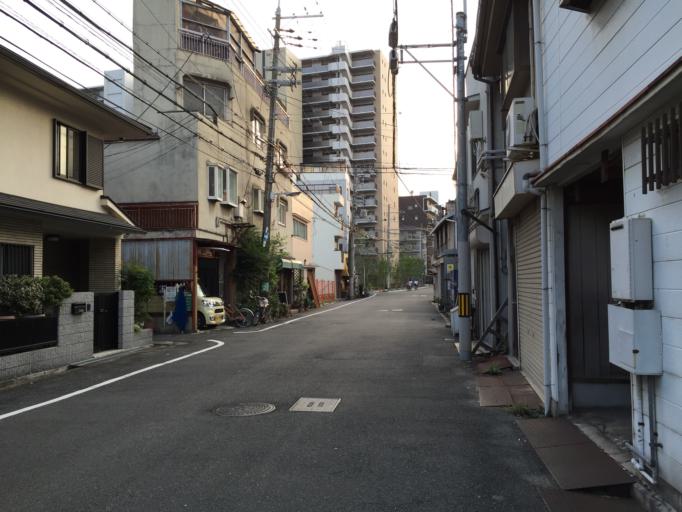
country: JP
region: Osaka
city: Osaka-shi
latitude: 34.7124
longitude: 135.4927
